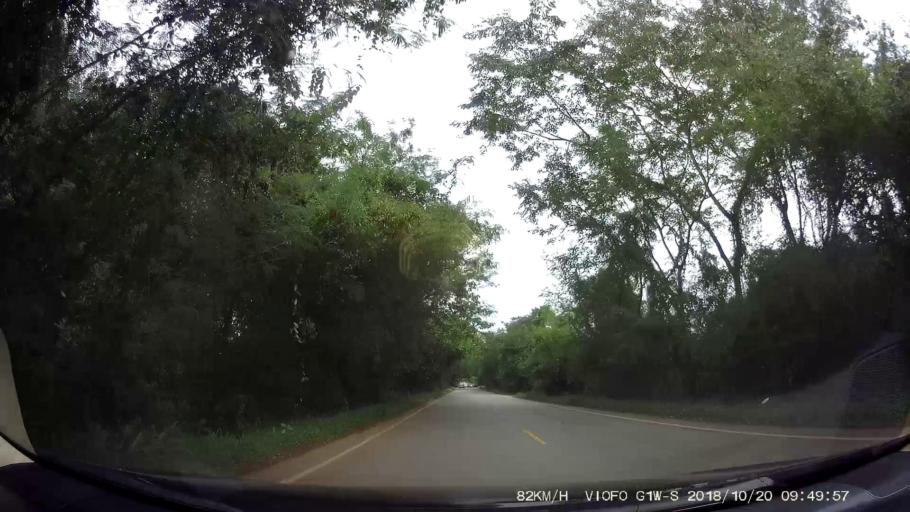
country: TH
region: Chaiyaphum
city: Khon San
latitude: 16.5256
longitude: 101.9036
